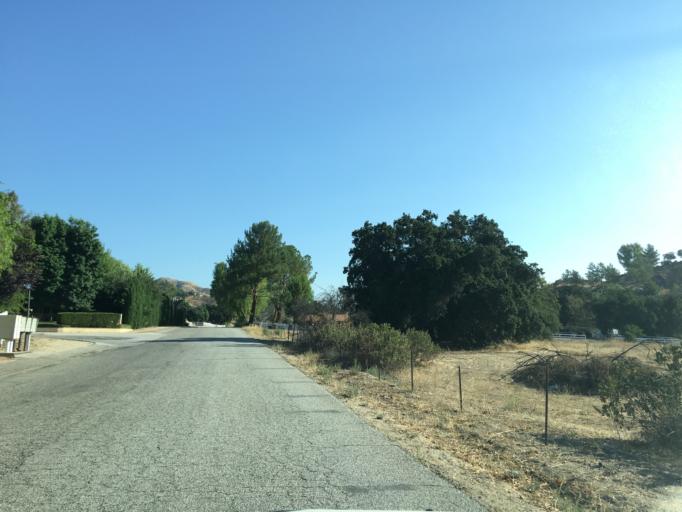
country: US
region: California
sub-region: Los Angeles County
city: Val Verde
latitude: 34.4688
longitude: -118.6605
